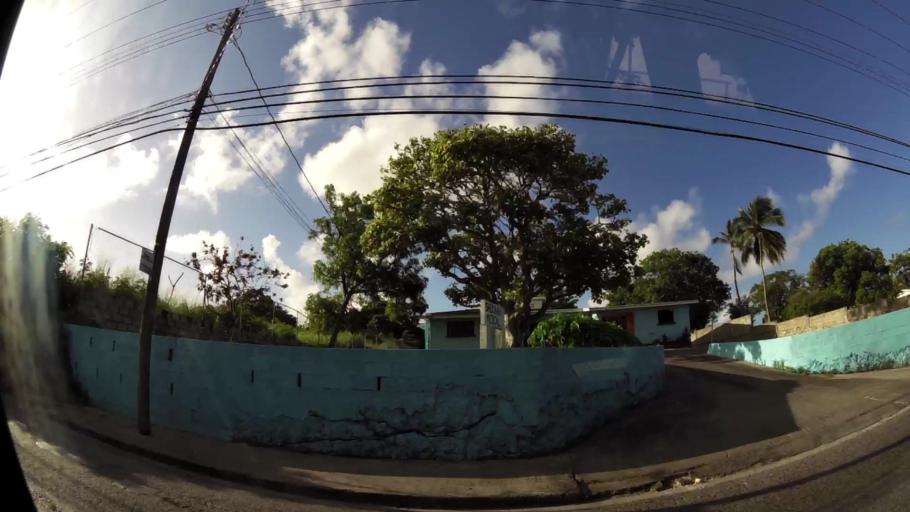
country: BB
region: Saint Michael
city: Bridgetown
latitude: 13.0920
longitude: -59.5886
